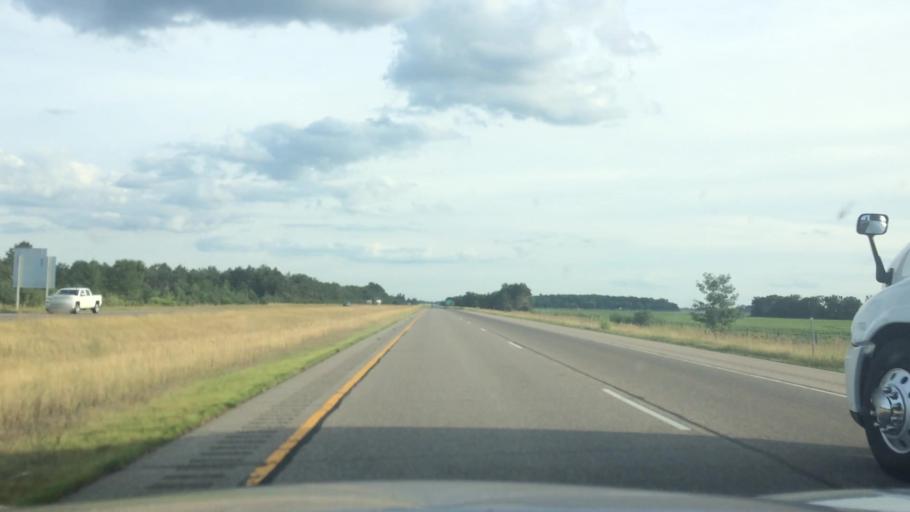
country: US
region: Wisconsin
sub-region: Portage County
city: Plover
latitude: 44.2415
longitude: -89.5243
